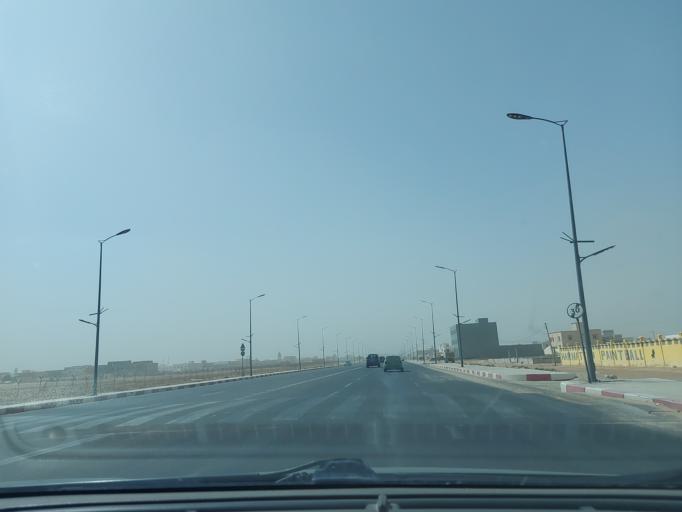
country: MR
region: Nouakchott
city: Nouakchott
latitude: 18.1362
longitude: -16.0051
